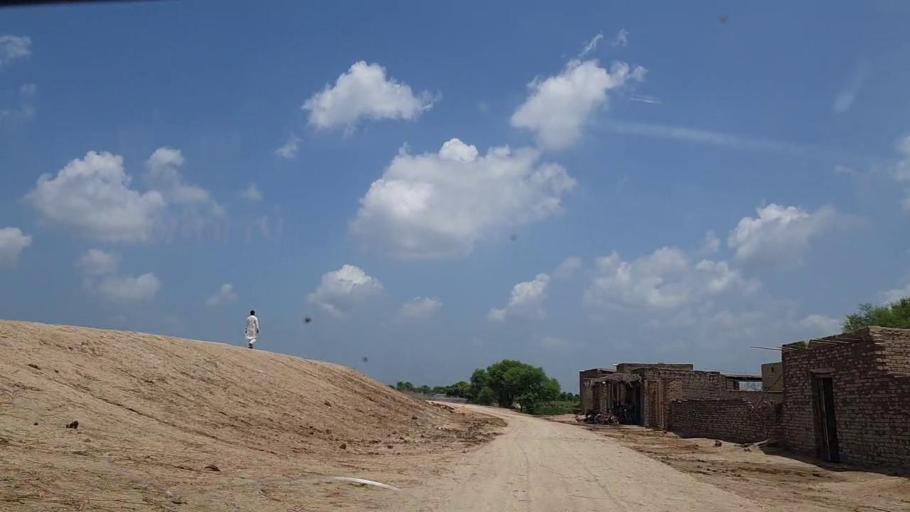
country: PK
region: Sindh
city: Tharu Shah
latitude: 26.9880
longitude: 68.0587
